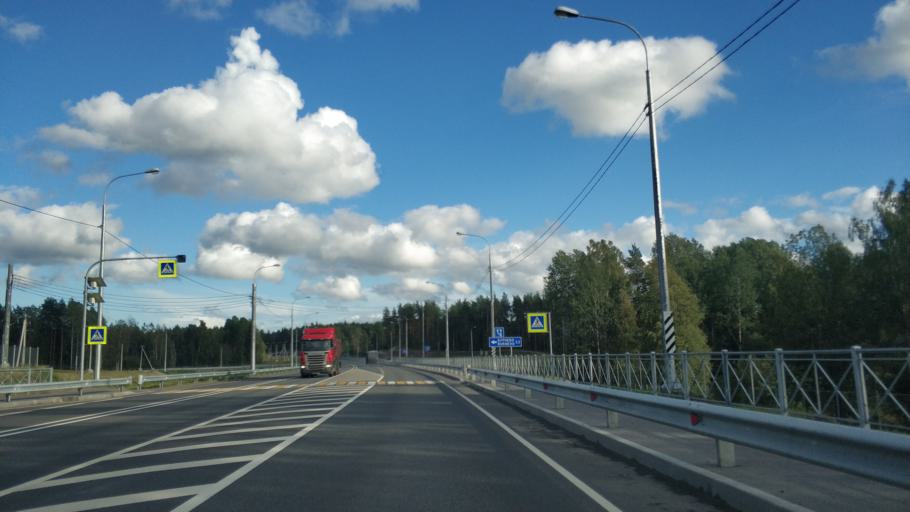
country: RU
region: Leningrad
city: Kuznechnoye
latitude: 61.0989
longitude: 29.9744
